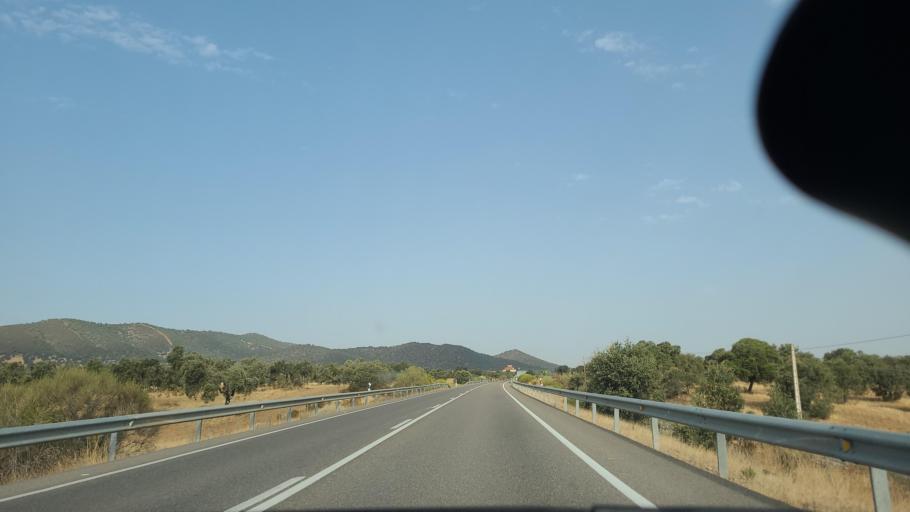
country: ES
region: Andalusia
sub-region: Province of Cordoba
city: Belmez
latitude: 38.2081
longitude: -5.1297
